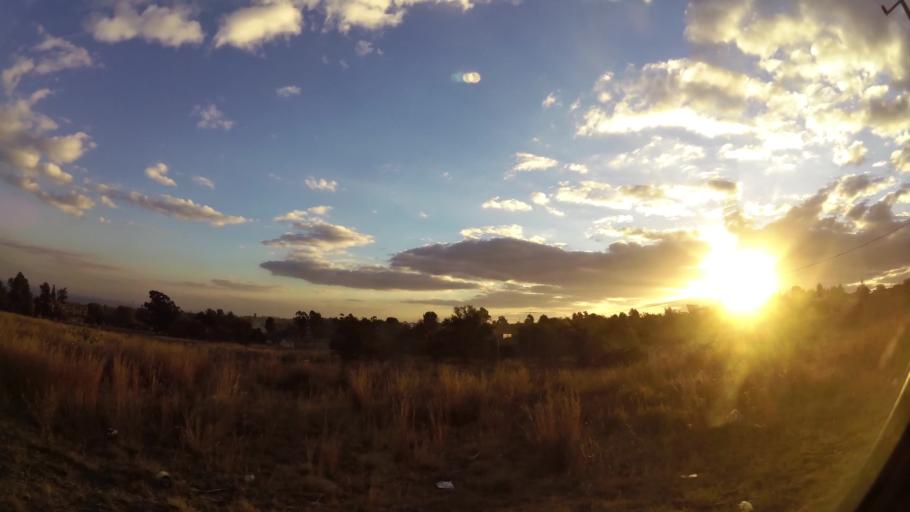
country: ZA
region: Gauteng
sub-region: City of Johannesburg Metropolitan Municipality
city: Midrand
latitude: -25.9975
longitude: 28.1503
